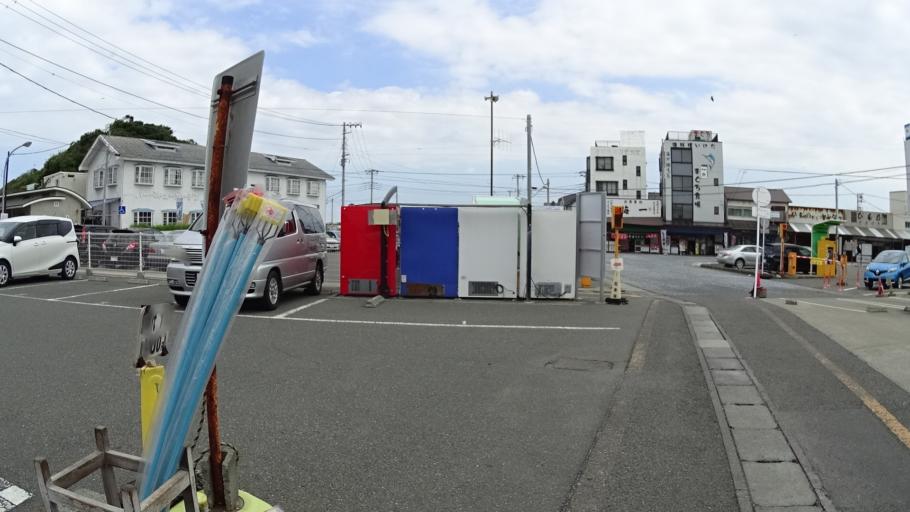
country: JP
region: Kanagawa
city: Miura
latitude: 35.1359
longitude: 139.6124
